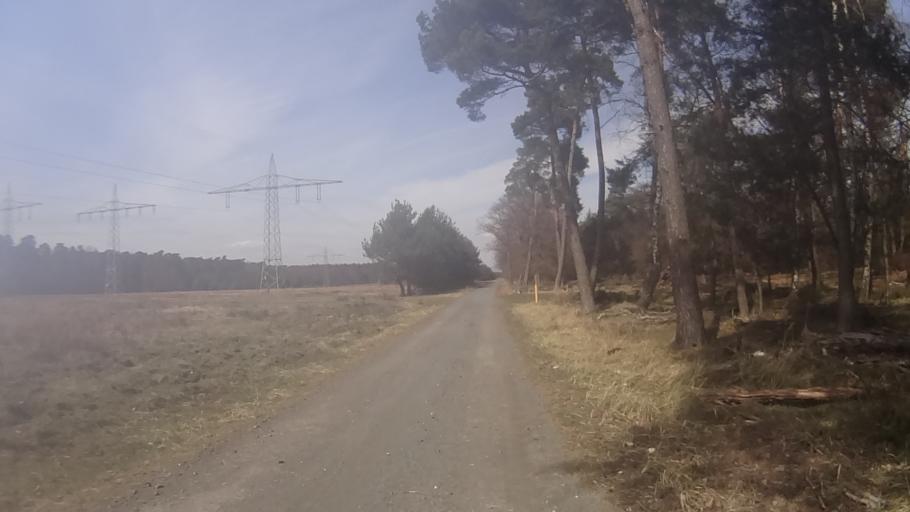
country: DE
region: Hesse
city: Kelsterbach
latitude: 50.0150
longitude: 8.5109
